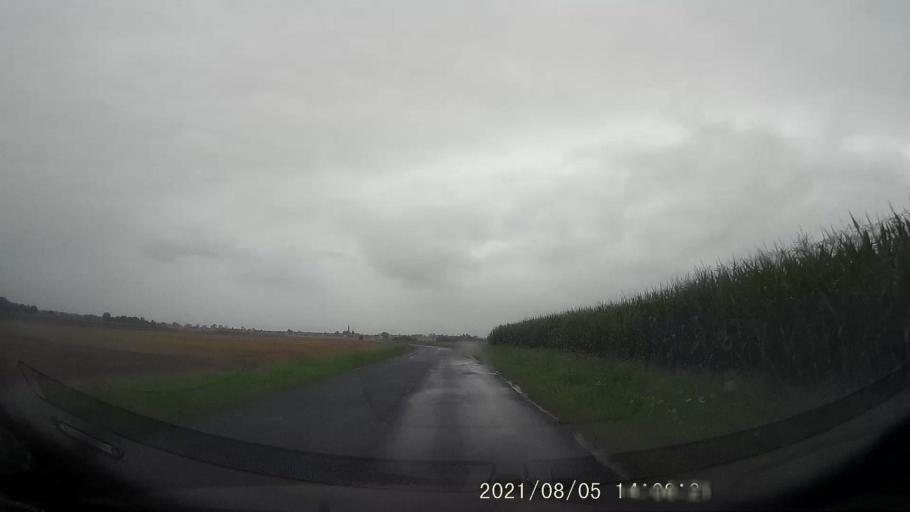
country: PL
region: Opole Voivodeship
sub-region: Powiat krapkowicki
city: Strzeleczki
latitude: 50.4693
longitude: 17.8178
